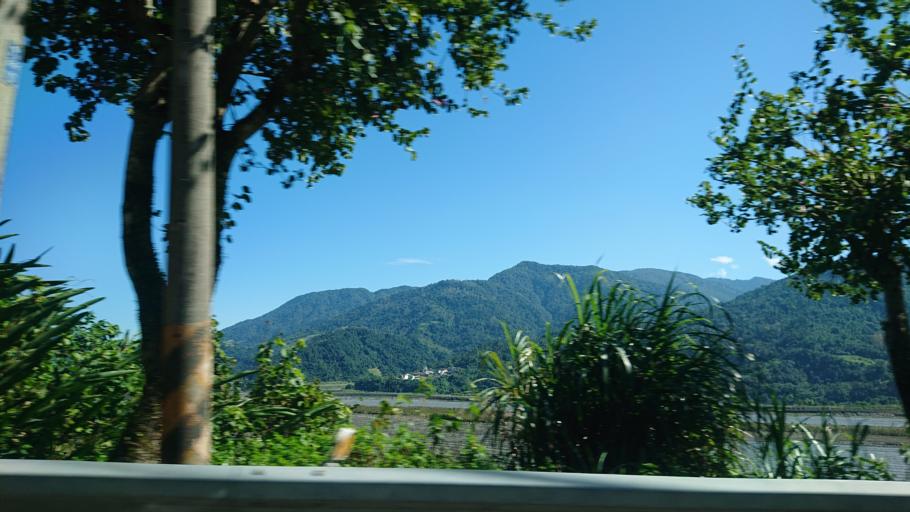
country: TW
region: Taiwan
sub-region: Yilan
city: Yilan
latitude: 24.5996
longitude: 121.5144
